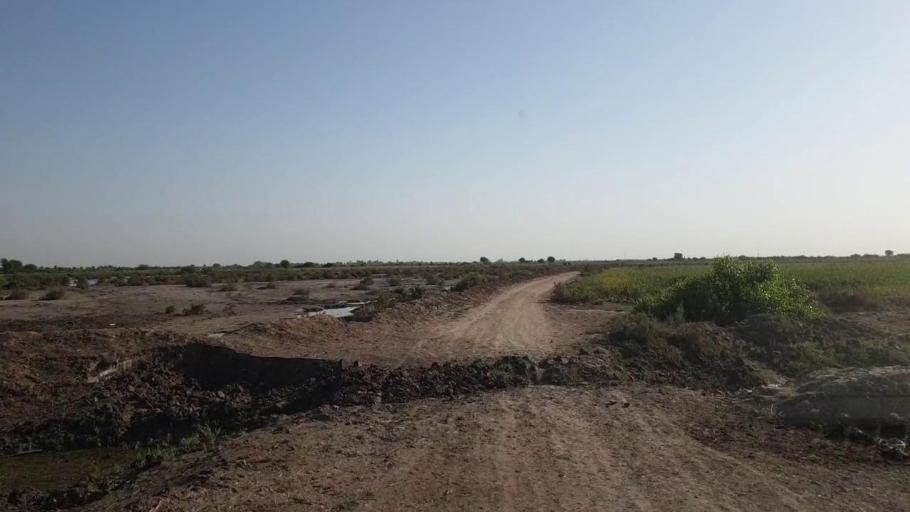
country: PK
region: Sindh
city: Badin
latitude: 24.5901
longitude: 68.9129
